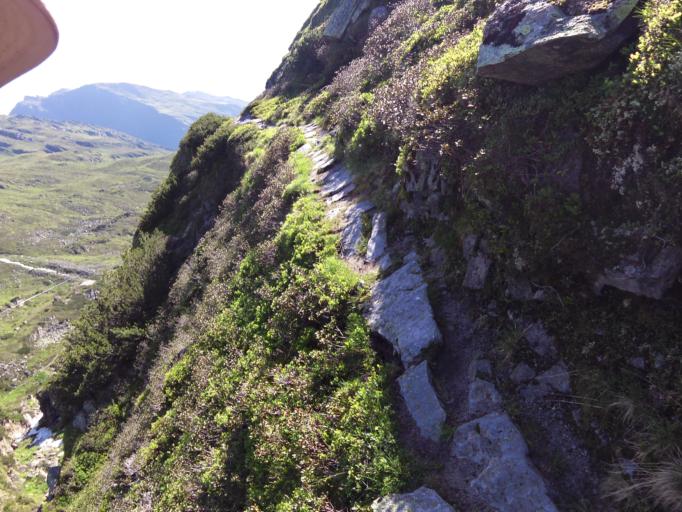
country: AT
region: Tyrol
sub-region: Politischer Bezirk Innsbruck Land
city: Gries im Sellrain
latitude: 47.0853
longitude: 11.1721
